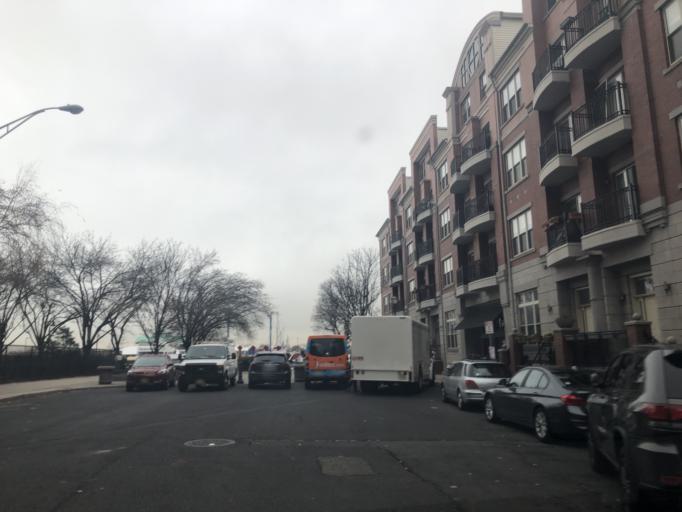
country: US
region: New Jersey
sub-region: Hudson County
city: Hoboken
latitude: 40.7118
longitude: -74.0401
